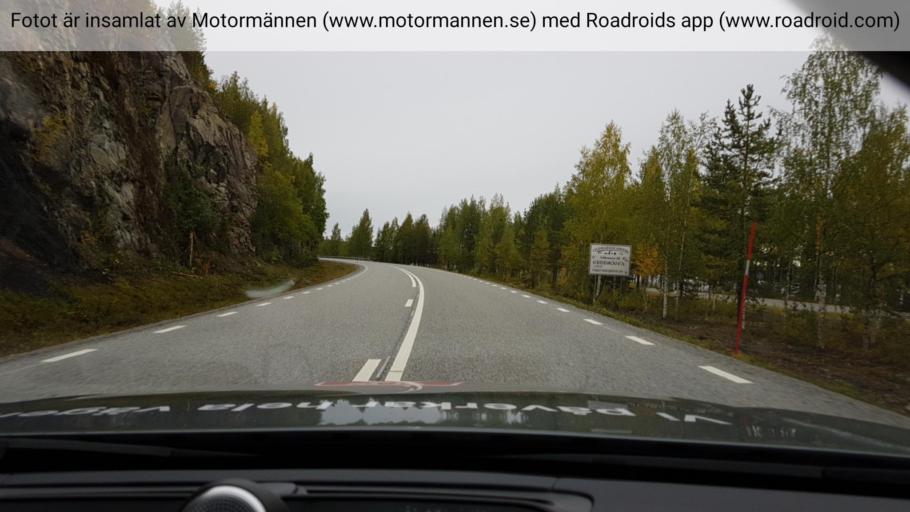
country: SE
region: Jaemtland
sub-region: Stroemsunds Kommun
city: Stroemsund
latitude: 64.1815
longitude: 15.6552
